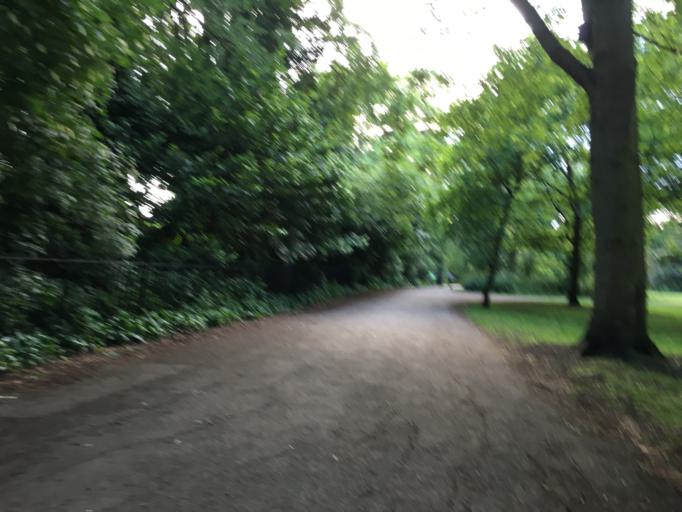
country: GB
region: England
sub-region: Greater London
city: Camden Town
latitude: 51.5295
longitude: -0.1493
